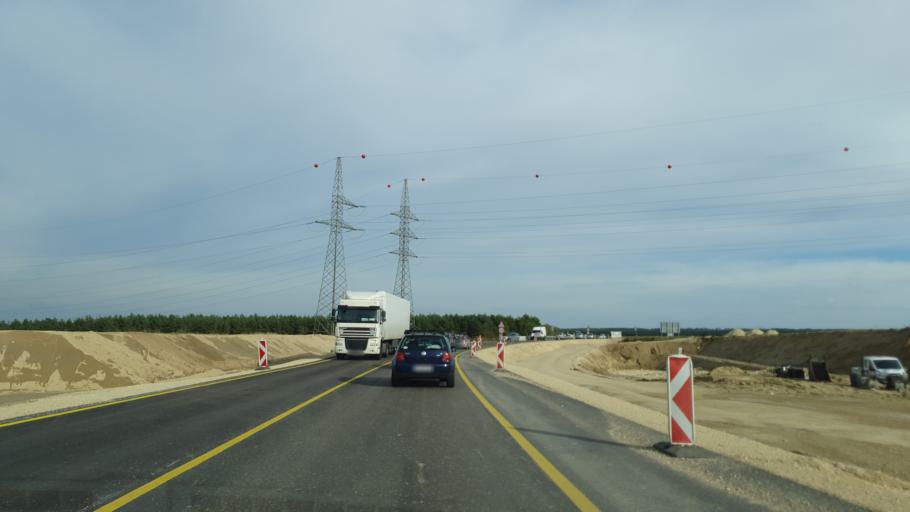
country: HU
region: Veszprem
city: Veszprem
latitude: 47.1020
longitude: 17.9404
